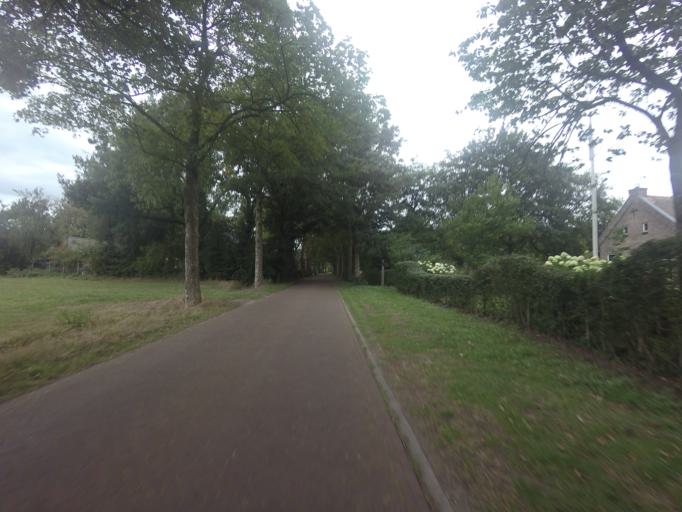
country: NL
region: Friesland
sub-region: Gemeente Heerenveen
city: Jubbega
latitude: 52.9749
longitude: 6.2534
